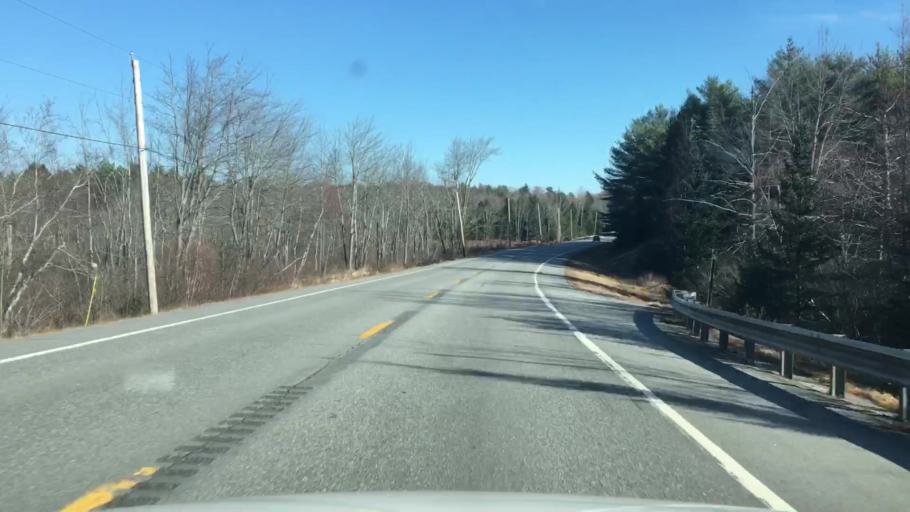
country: US
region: Maine
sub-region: Lincoln County
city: Jefferson
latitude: 44.2565
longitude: -69.4802
